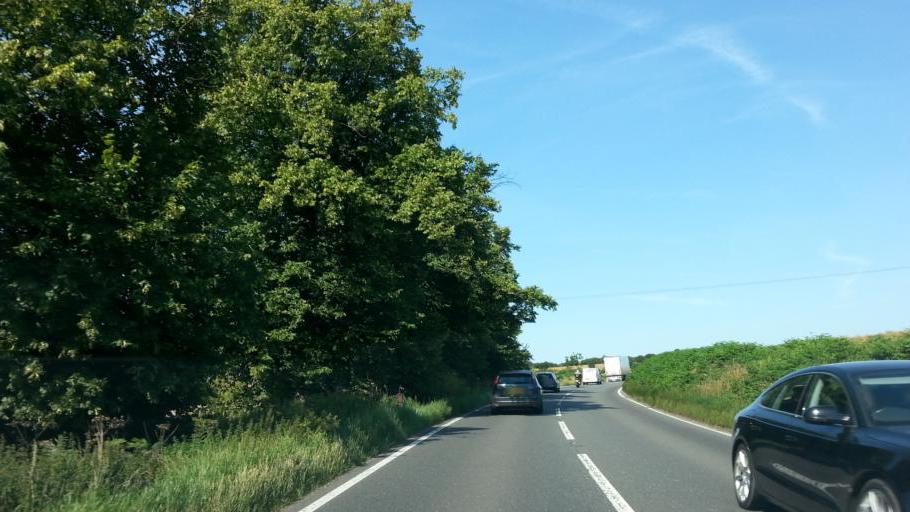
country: GB
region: England
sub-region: Nottinghamshire
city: Bilsthorpe
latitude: 53.1225
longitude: -1.0250
